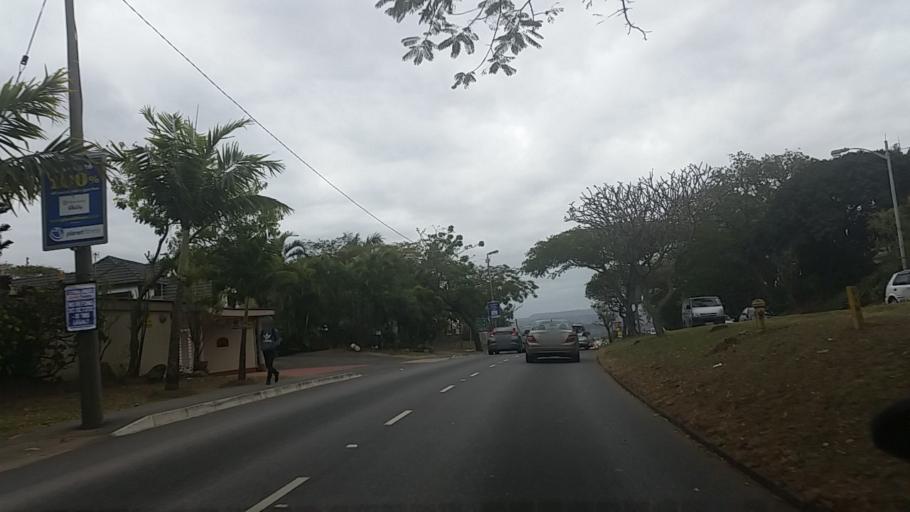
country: ZA
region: KwaZulu-Natal
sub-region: eThekwini Metropolitan Municipality
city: Berea
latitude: -29.8346
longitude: 30.9691
